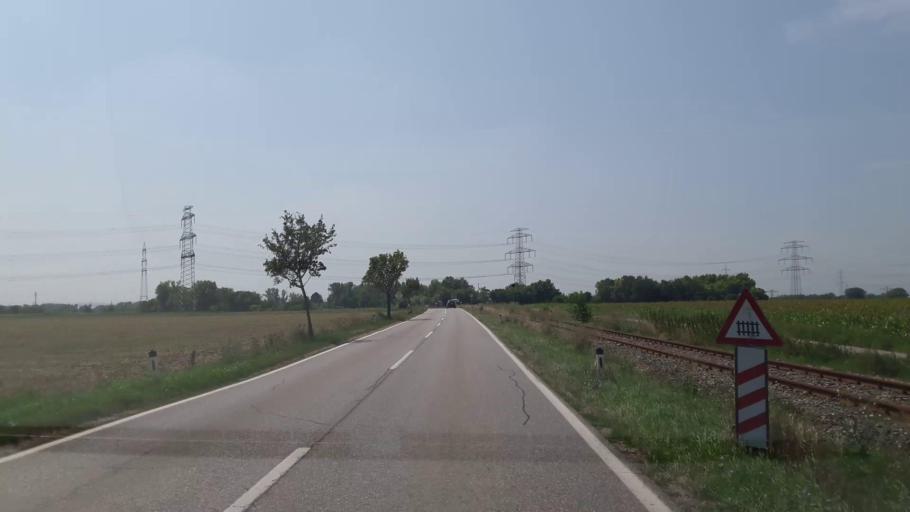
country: AT
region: Lower Austria
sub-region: Politischer Bezirk Bruck an der Leitha
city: Gotzendorf an der Leitha
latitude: 48.0311
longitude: 16.5953
